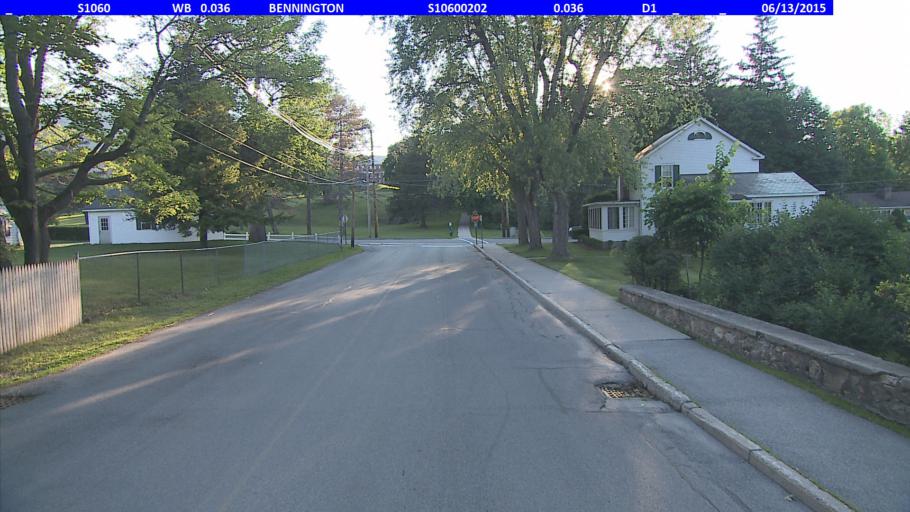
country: US
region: Vermont
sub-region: Bennington County
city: Bennington
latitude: 42.8747
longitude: -73.2033
